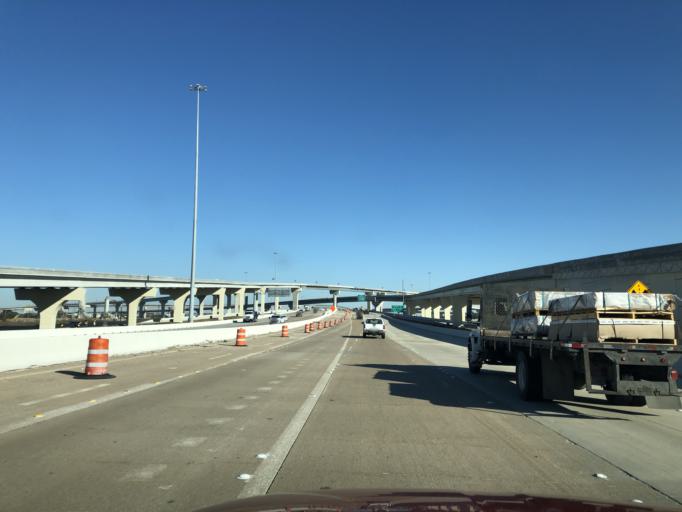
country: US
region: Texas
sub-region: Brazoria County
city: Brookside Village
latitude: 29.5964
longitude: -95.3954
